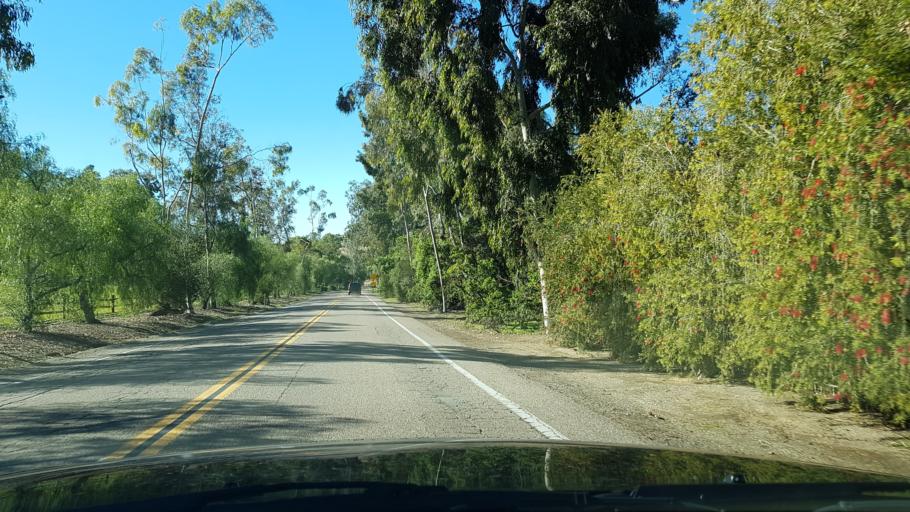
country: US
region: California
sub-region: San Diego County
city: Rancho Santa Fe
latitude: 33.0372
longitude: -117.2032
